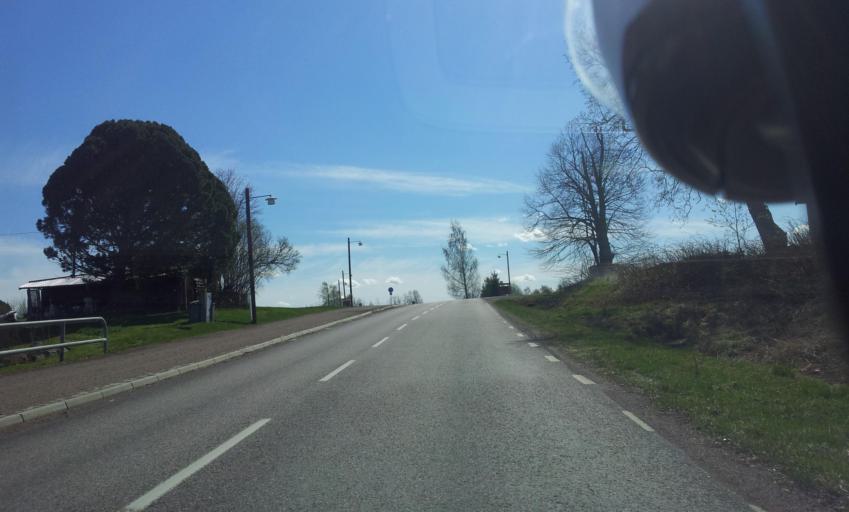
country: SE
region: Dalarna
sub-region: Borlange Kommun
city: Ornas
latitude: 60.4724
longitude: 15.5064
